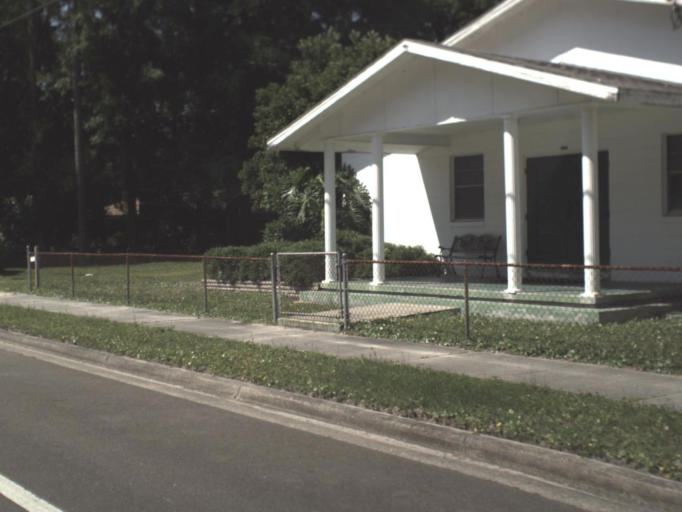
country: US
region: Florida
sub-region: Nassau County
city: Nassau Village-Ratliff
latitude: 30.4471
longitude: -81.7030
